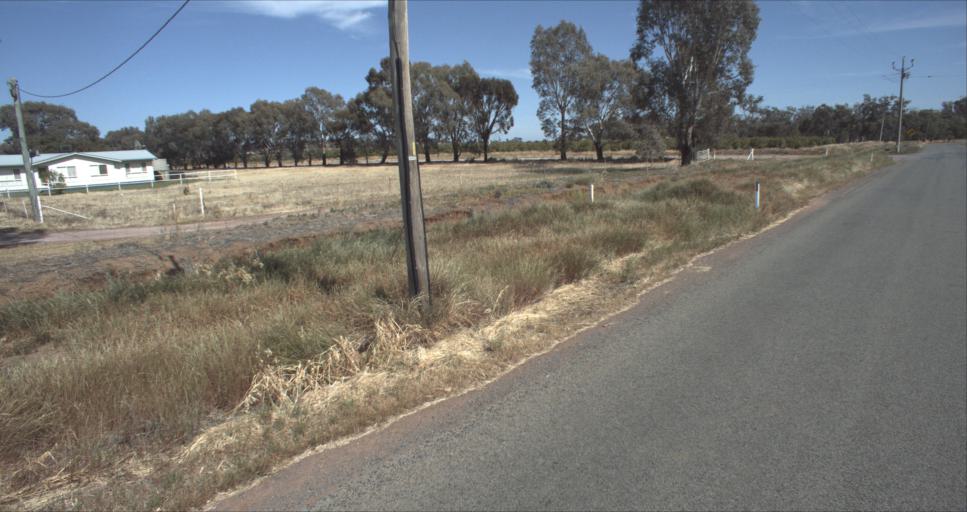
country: AU
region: New South Wales
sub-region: Leeton
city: Leeton
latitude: -34.5786
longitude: 146.4681
